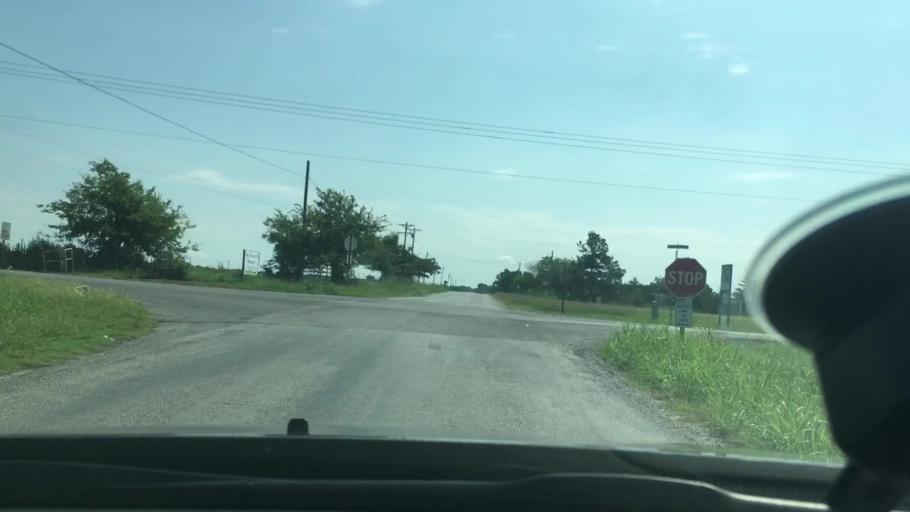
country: US
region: Oklahoma
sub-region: Bryan County
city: Colbert
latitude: 33.9110
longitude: -96.5009
